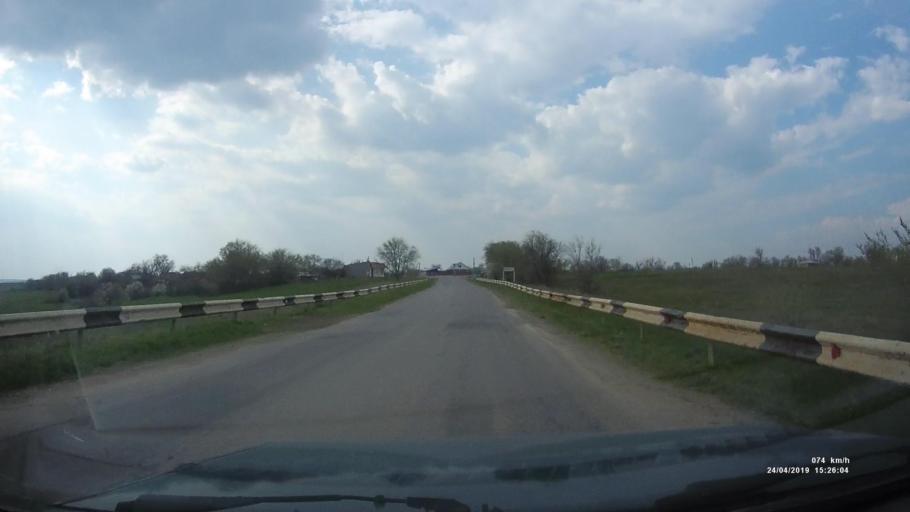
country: RU
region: Rostov
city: Remontnoye
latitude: 46.5561
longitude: 43.0376
